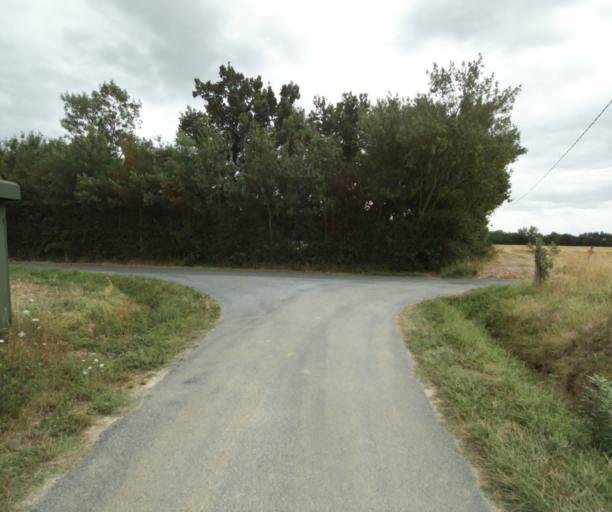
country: FR
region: Midi-Pyrenees
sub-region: Departement du Tarn
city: Soreze
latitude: 43.4709
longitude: 2.0406
